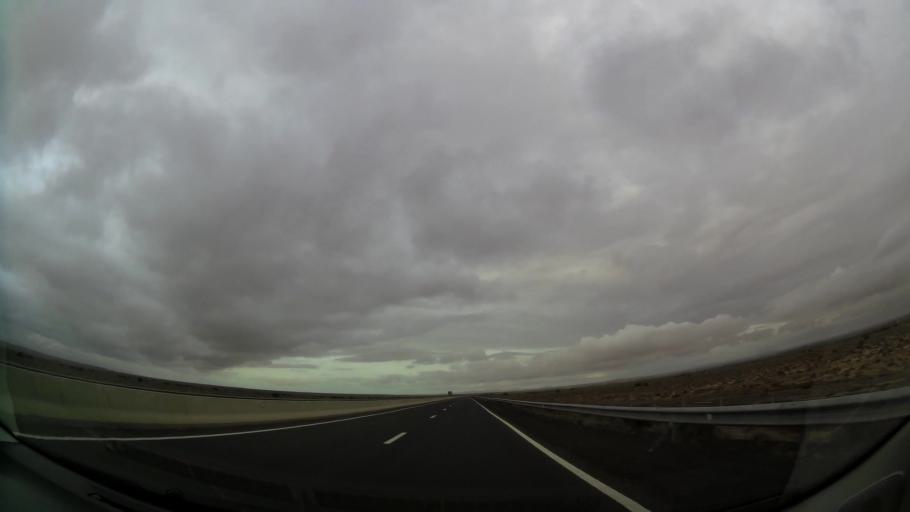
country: MA
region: Taza-Al Hoceima-Taounate
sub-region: Taza
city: Guercif
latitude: 34.3718
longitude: -3.2672
